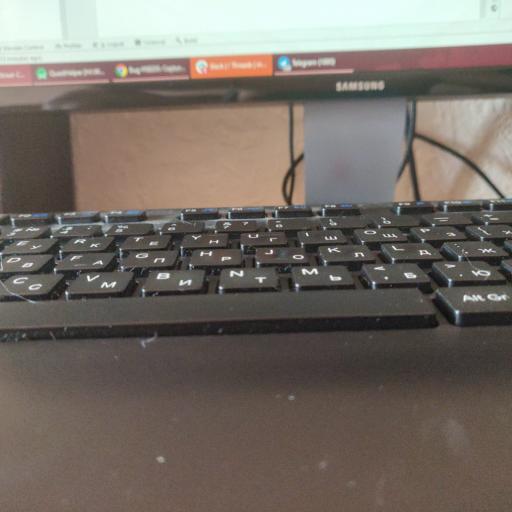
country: FI
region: Haeme
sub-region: Forssa
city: Jokioinen
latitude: 60.7997
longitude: 23.4588
